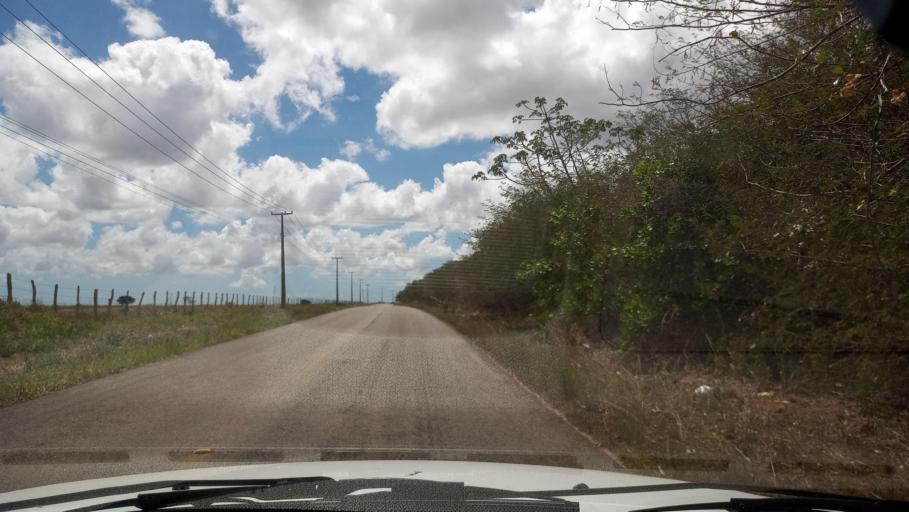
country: BR
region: Rio Grande do Norte
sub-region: Brejinho
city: Brejinho
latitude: -6.0417
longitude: -35.4211
